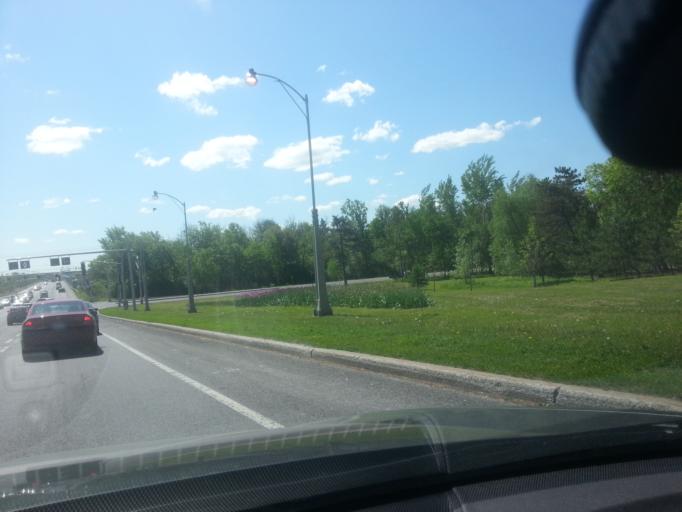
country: CA
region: Ontario
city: Ottawa
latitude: 45.4134
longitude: -75.7659
